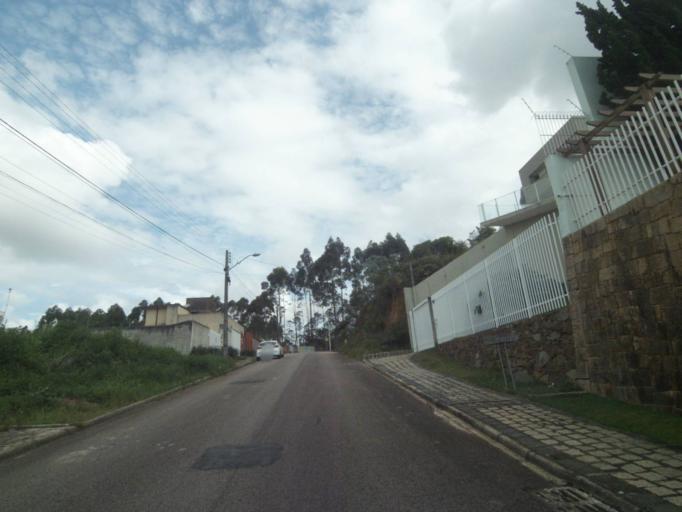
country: BR
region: Parana
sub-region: Curitiba
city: Curitiba
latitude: -25.3802
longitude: -49.2873
